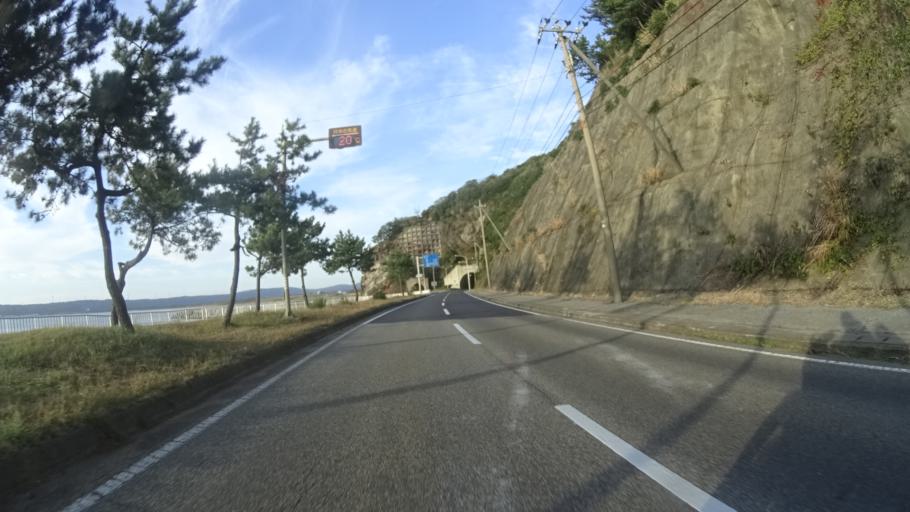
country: JP
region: Ishikawa
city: Nanao
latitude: 37.1306
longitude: 136.7270
